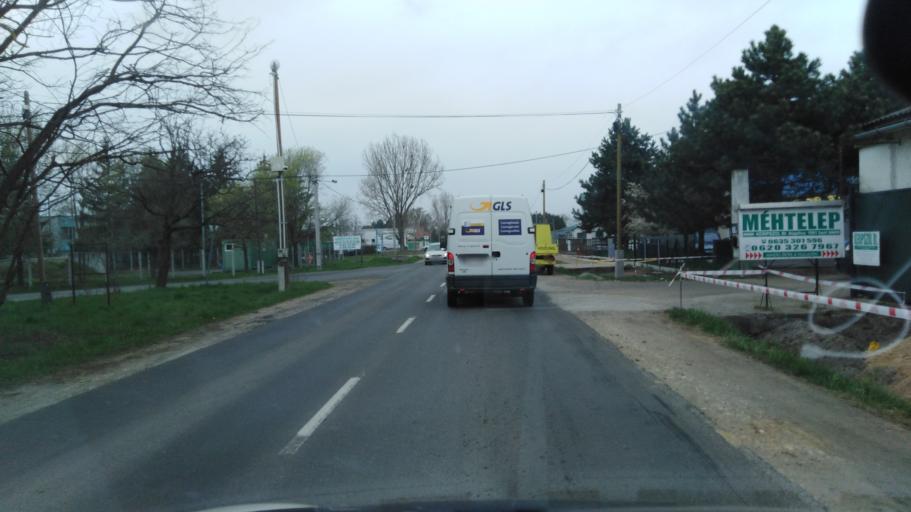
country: HU
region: Nograd
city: Balassagyarmat
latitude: 48.0609
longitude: 19.3048
